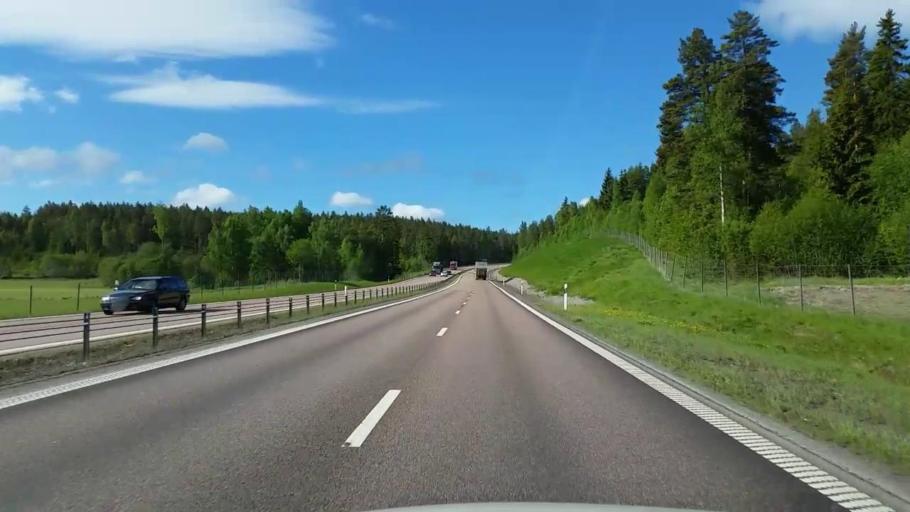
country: SE
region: Dalarna
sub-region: Borlange Kommun
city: Ornas
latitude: 60.5439
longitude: 15.5645
